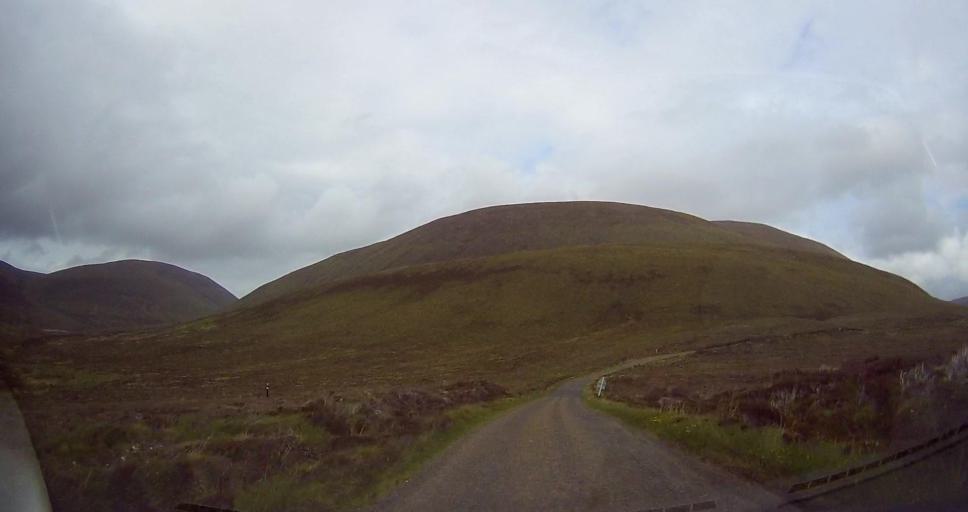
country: GB
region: Scotland
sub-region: Orkney Islands
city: Stromness
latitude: 58.8814
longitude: -3.3818
